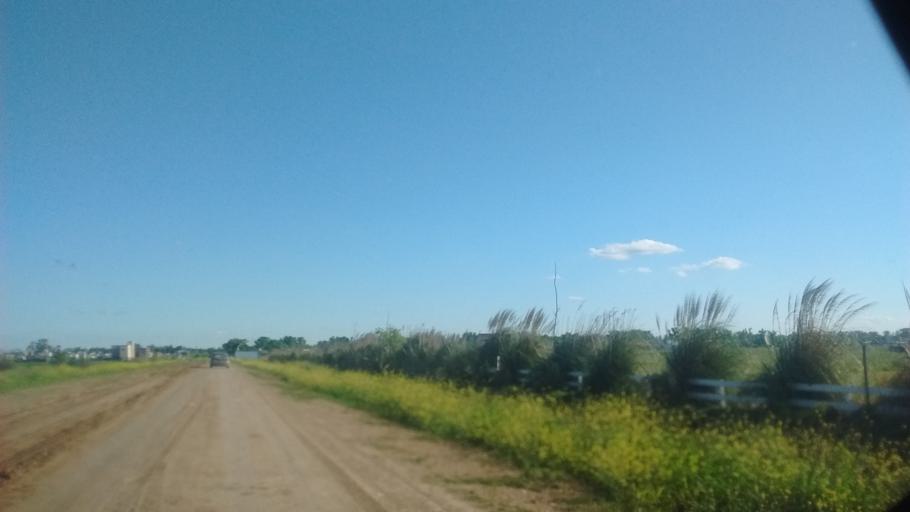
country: AR
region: Santa Fe
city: Funes
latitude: -32.8966
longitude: -60.8052
